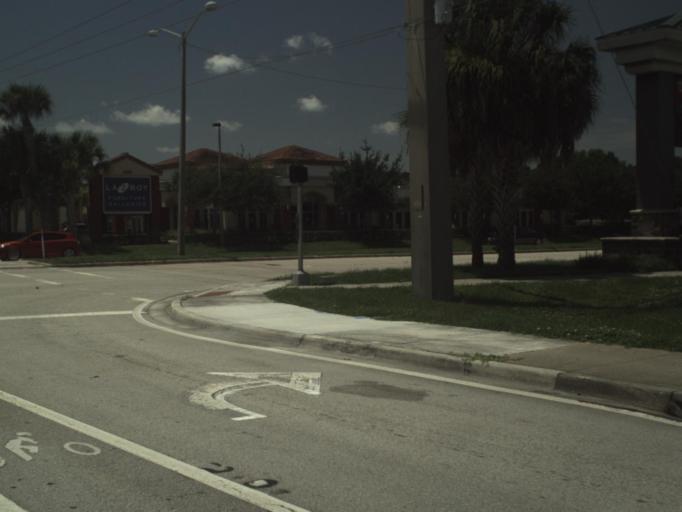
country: US
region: Florida
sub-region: Martin County
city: North River Shores
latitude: 27.2595
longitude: -80.2817
